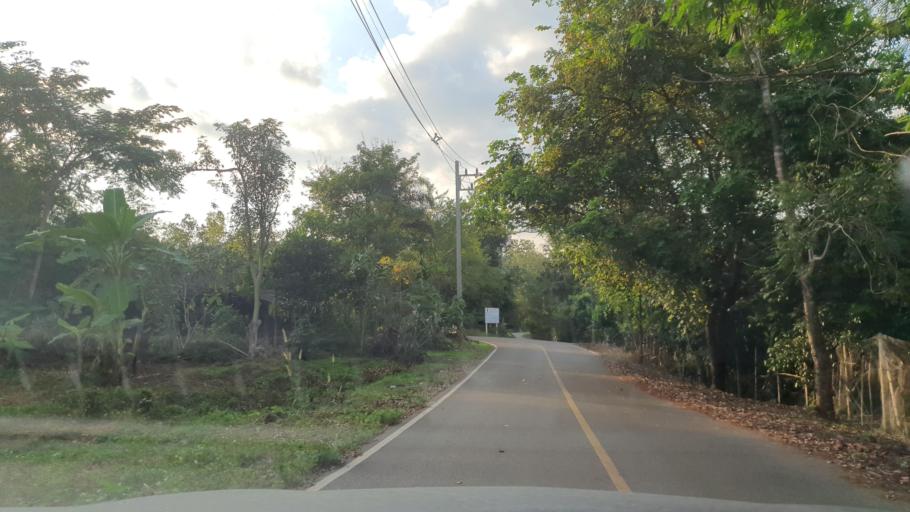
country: TH
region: Chiang Mai
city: Mae On
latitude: 18.8693
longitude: 99.2417
